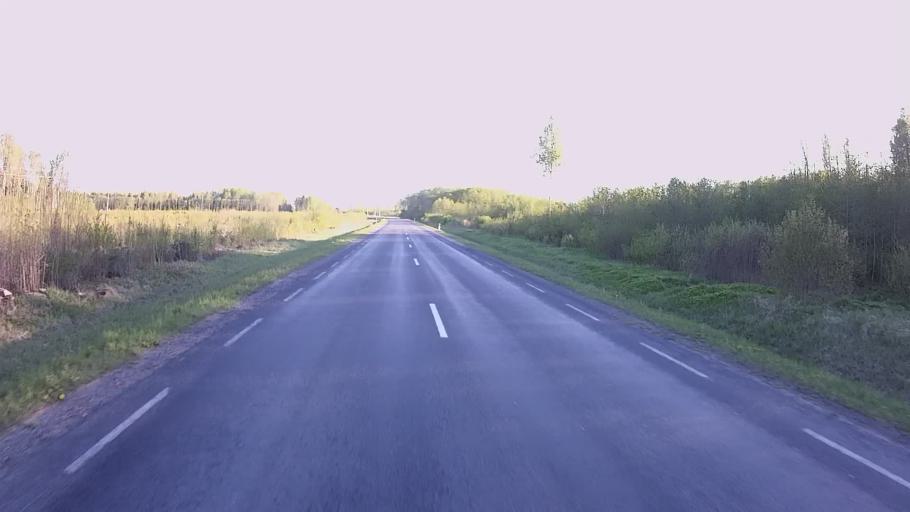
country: EE
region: Viljandimaa
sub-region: Viiratsi vald
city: Viiratsi
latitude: 58.4576
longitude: 25.7478
